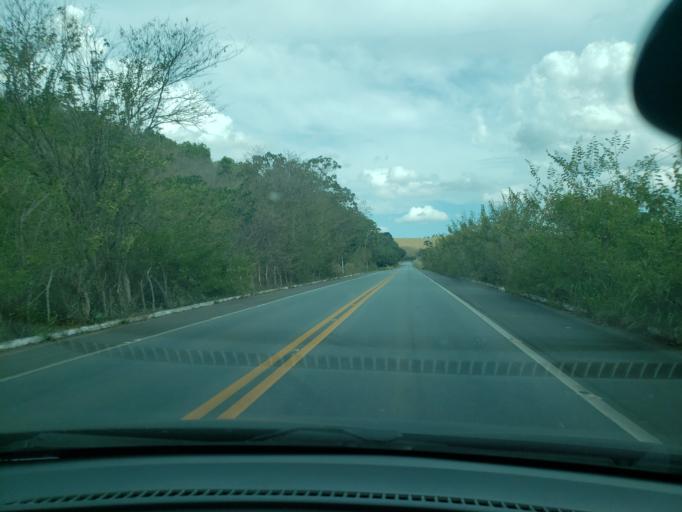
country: BR
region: Alagoas
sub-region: Murici
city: Murici
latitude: -9.2593
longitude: -35.9750
